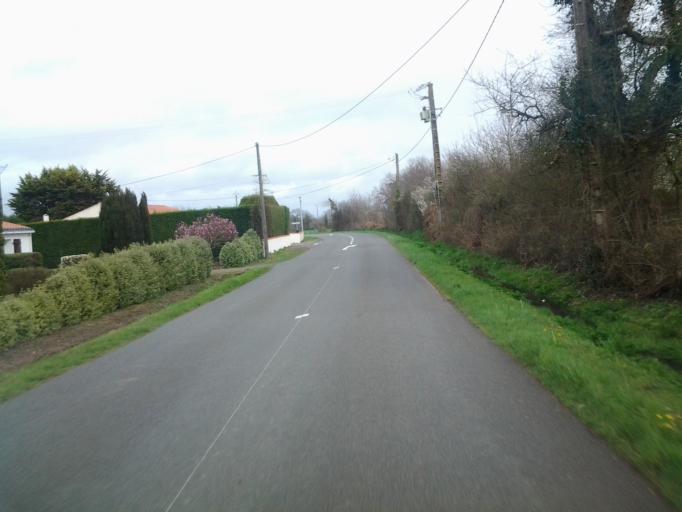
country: FR
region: Pays de la Loire
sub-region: Departement de la Vendee
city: Moutiers-les-Mauxfaits
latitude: 46.4990
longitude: -1.4531
